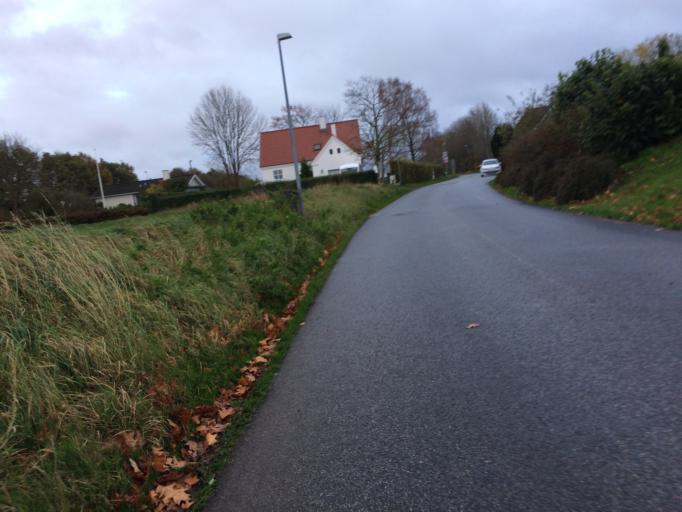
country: DK
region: South Denmark
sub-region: Vejle Kommune
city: Borkop
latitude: 55.6061
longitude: 9.6461
